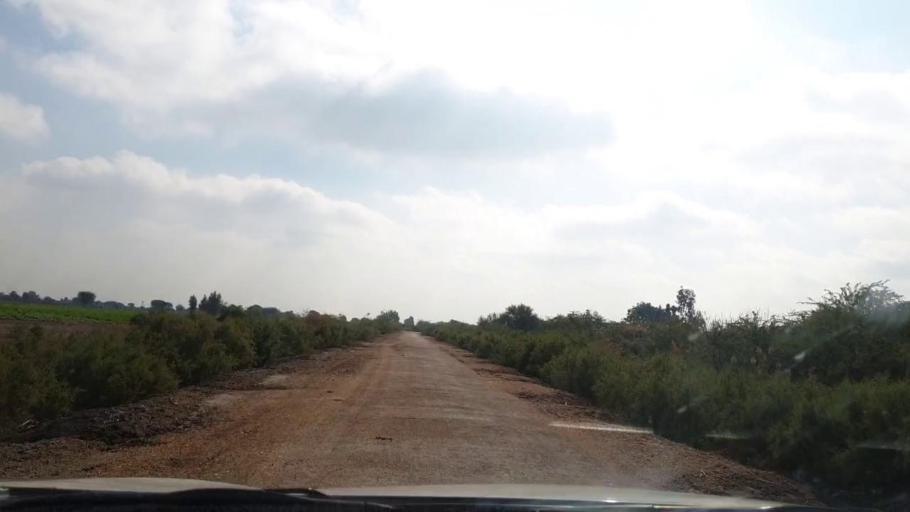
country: PK
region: Sindh
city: Berani
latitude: 25.7823
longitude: 68.9669
